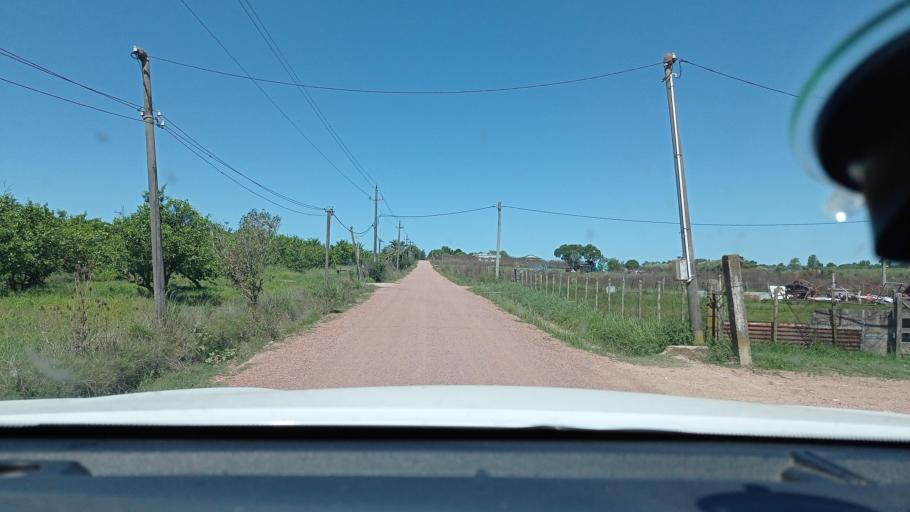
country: UY
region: Canelones
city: La Paz
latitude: -34.7475
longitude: -56.2023
